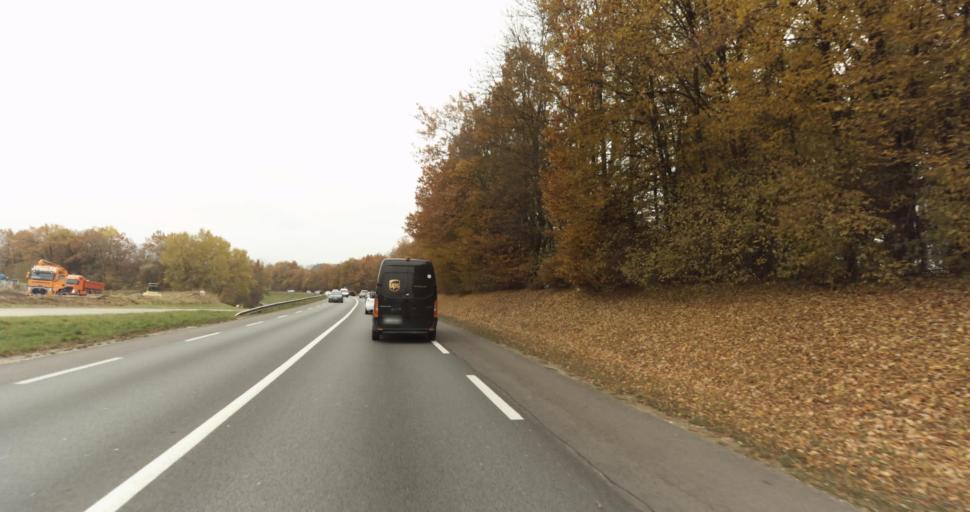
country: FR
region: Rhone-Alpes
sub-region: Departement de la Haute-Savoie
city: Meythet
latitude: 45.9128
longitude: 6.0823
